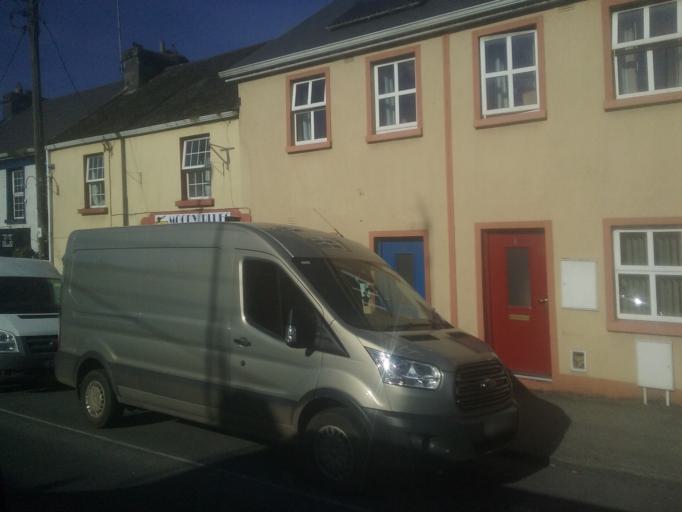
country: IE
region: Connaught
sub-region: County Galway
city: Gort
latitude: 53.0639
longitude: -8.8151
